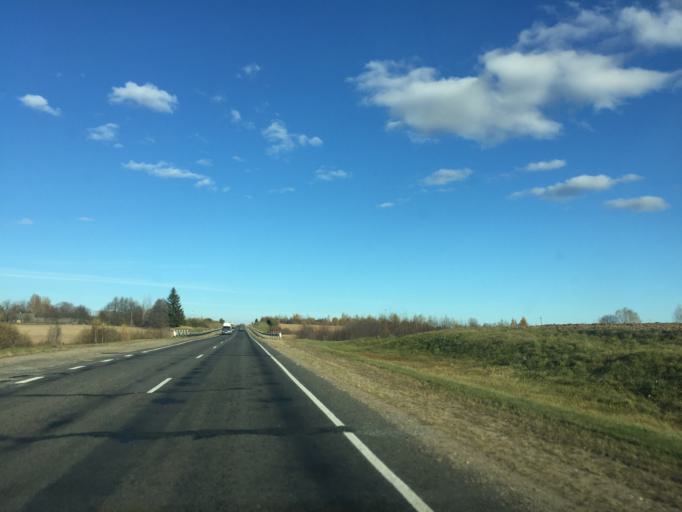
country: BY
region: Vitebsk
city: Dzisna
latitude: 55.2812
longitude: 28.1702
